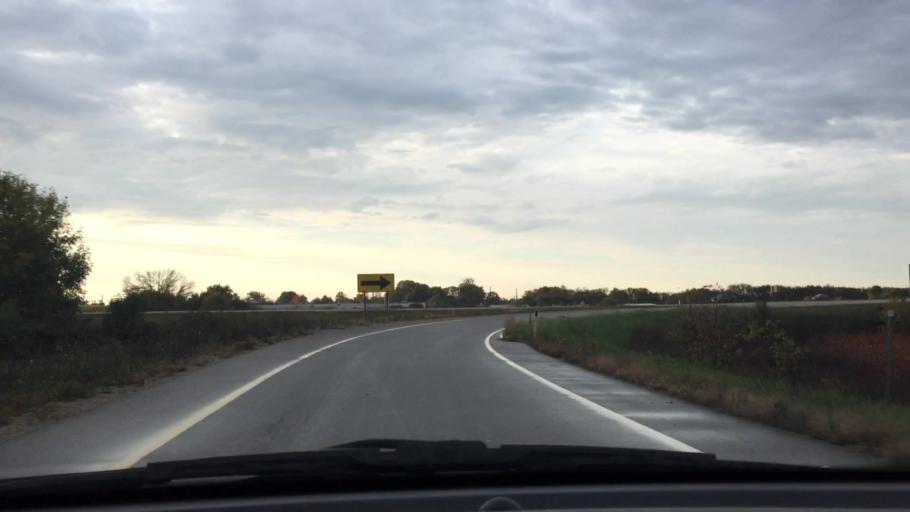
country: US
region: Wisconsin
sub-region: Walworth County
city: Elkhorn
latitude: 42.6736
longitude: -88.5243
